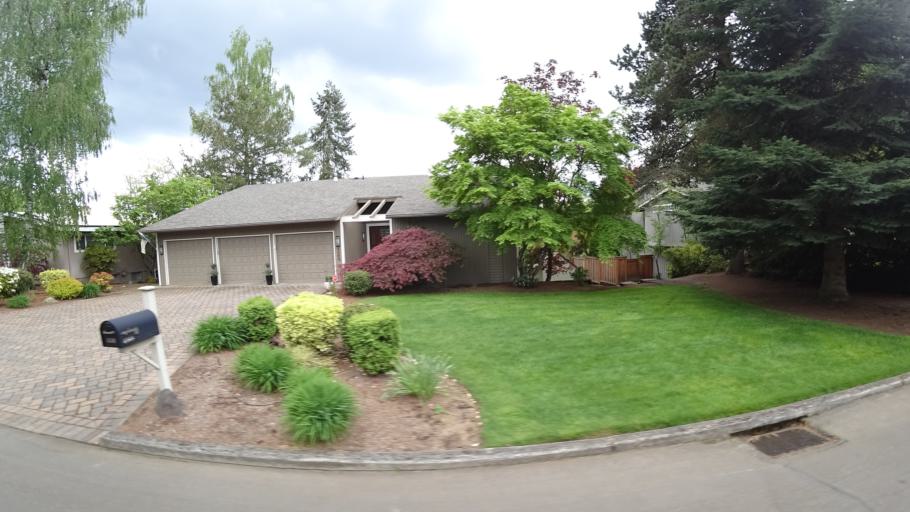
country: US
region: Oregon
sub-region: Washington County
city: Rockcreek
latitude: 45.5521
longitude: -122.8812
